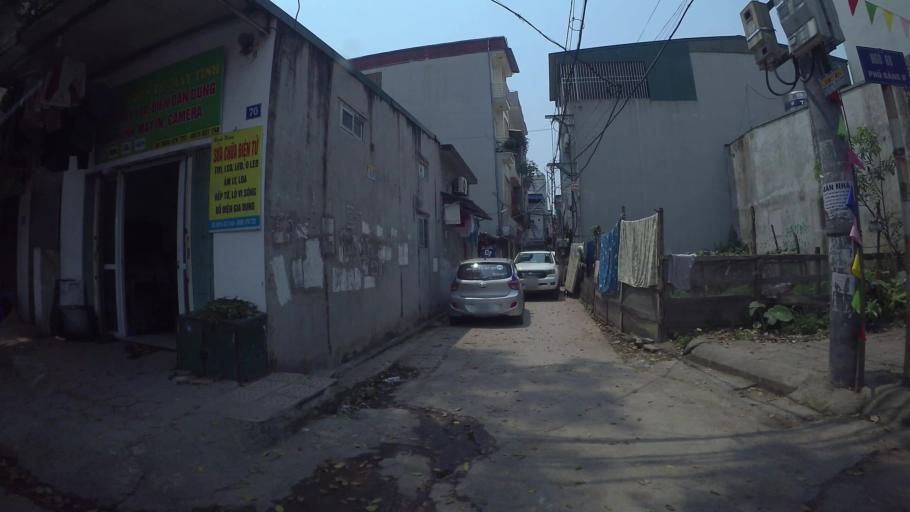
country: VN
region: Ha Noi
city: Van Dien
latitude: 20.9544
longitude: 105.8304
